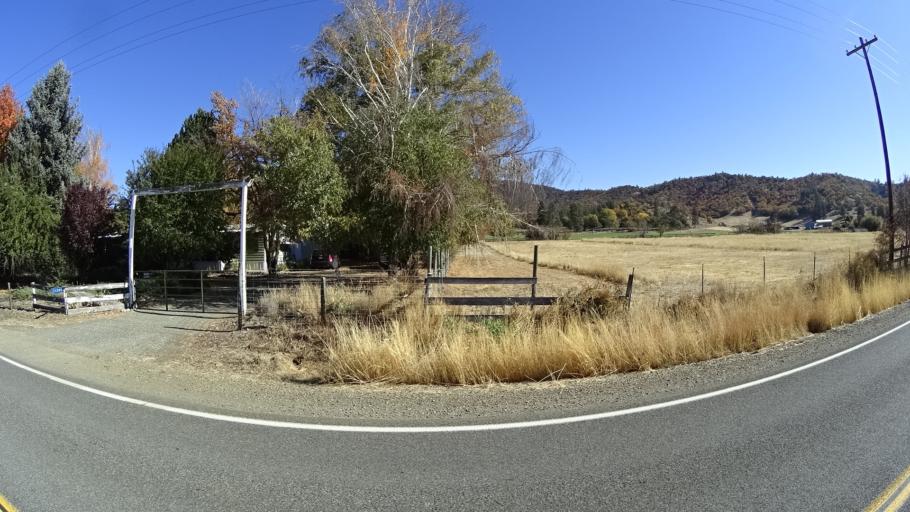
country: US
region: California
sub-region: Siskiyou County
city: Yreka
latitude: 41.5930
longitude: -122.8398
